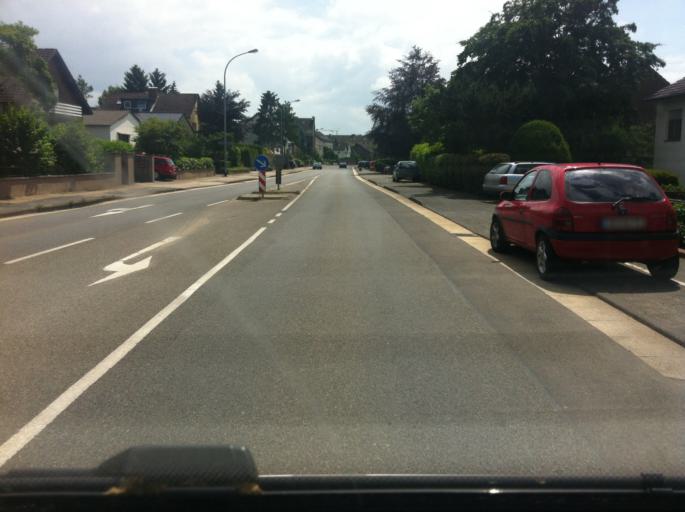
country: DE
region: North Rhine-Westphalia
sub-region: Regierungsbezirk Koln
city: Weilerswist
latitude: 50.7456
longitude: 6.8371
